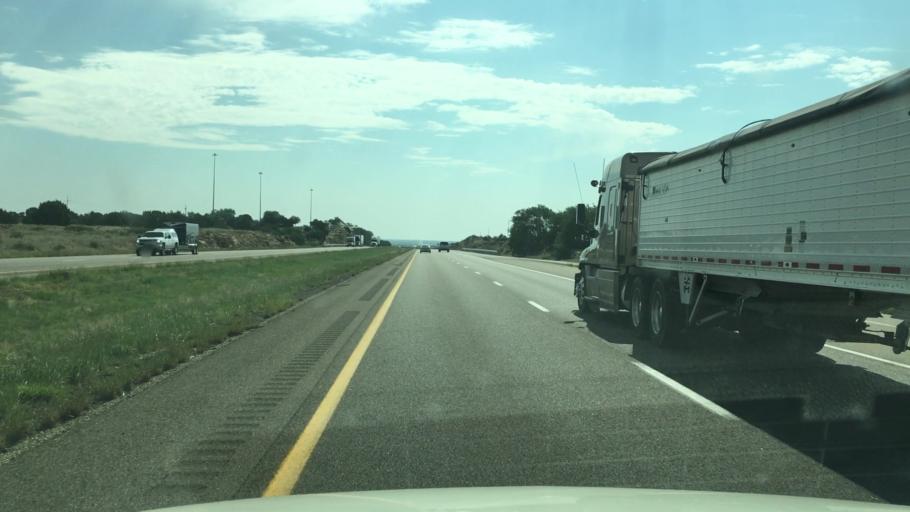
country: US
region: New Mexico
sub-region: Guadalupe County
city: Santa Rosa
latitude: 34.9812
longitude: -105.0860
